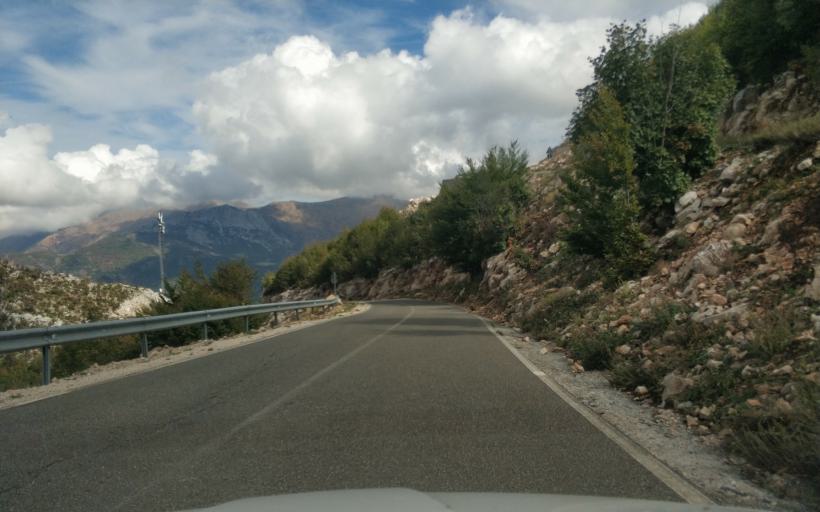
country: AL
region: Durres
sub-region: Rrethi i Krujes
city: Kruje
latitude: 41.5236
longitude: 19.8073
